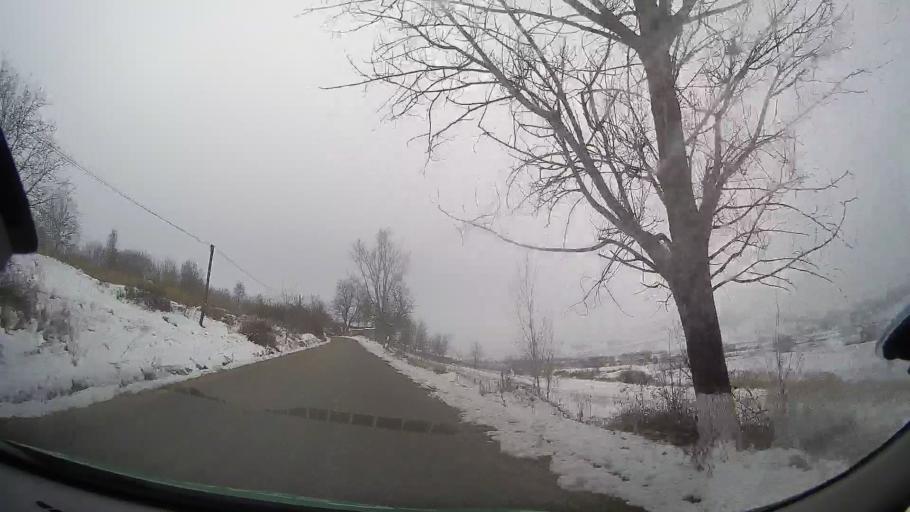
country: RO
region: Bacau
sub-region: Comuna Huruesti
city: Huruesti
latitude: 46.3070
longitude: 27.2933
